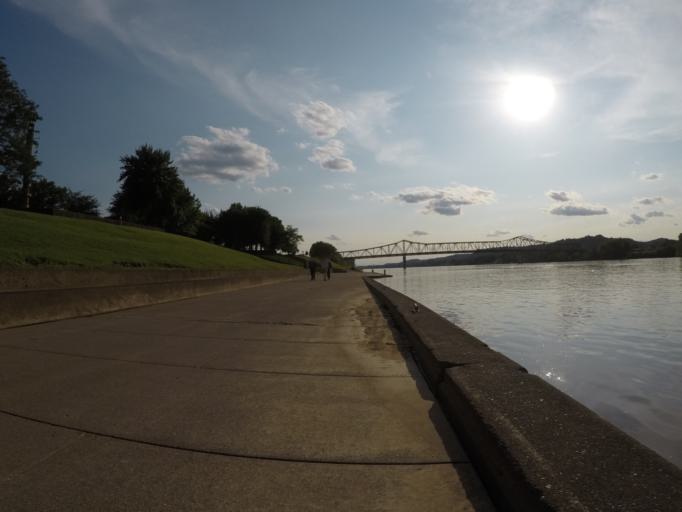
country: US
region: West Virginia
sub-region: Cabell County
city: Huntington
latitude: 38.4247
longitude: -82.4428
